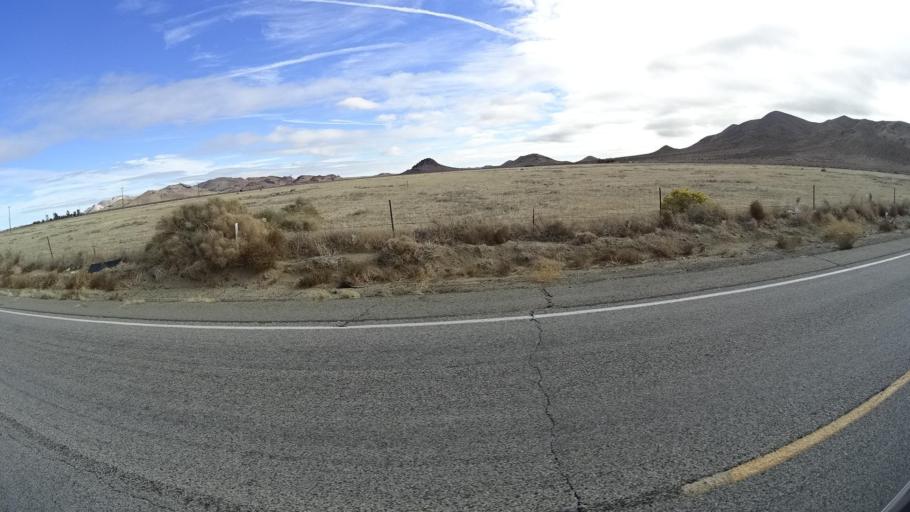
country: US
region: California
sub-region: Kern County
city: Rosamond
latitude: 34.8950
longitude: -118.2911
